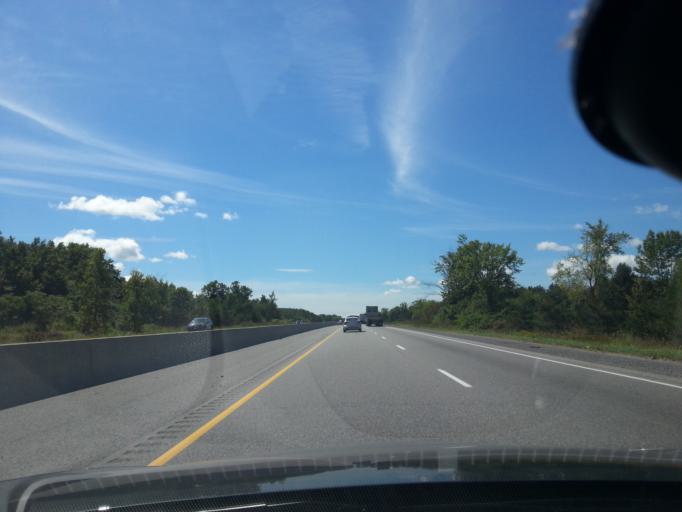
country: CA
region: Ontario
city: Gananoque
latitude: 44.3355
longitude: -76.2181
